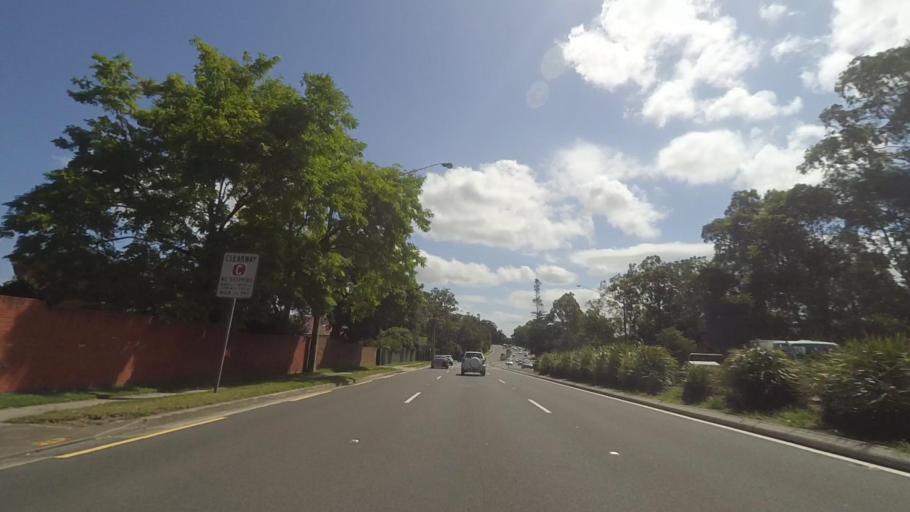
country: AU
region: New South Wales
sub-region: Ku-ring-gai
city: Normanhurst
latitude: -33.7227
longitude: 151.1020
